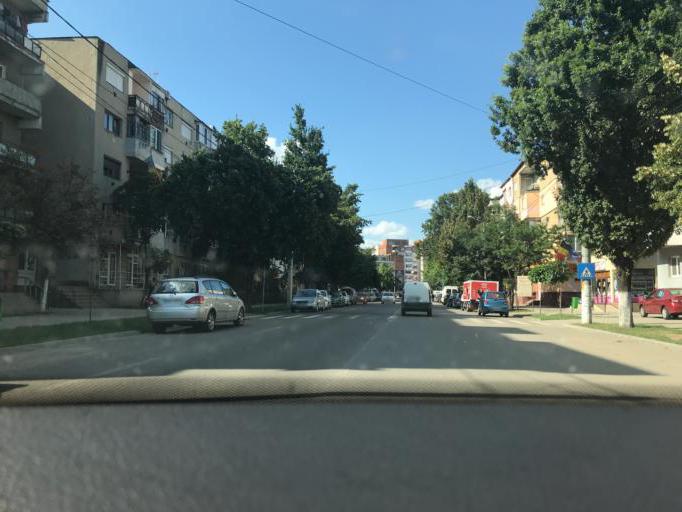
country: RO
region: Bihor
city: Margita
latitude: 47.3413
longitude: 22.3310
